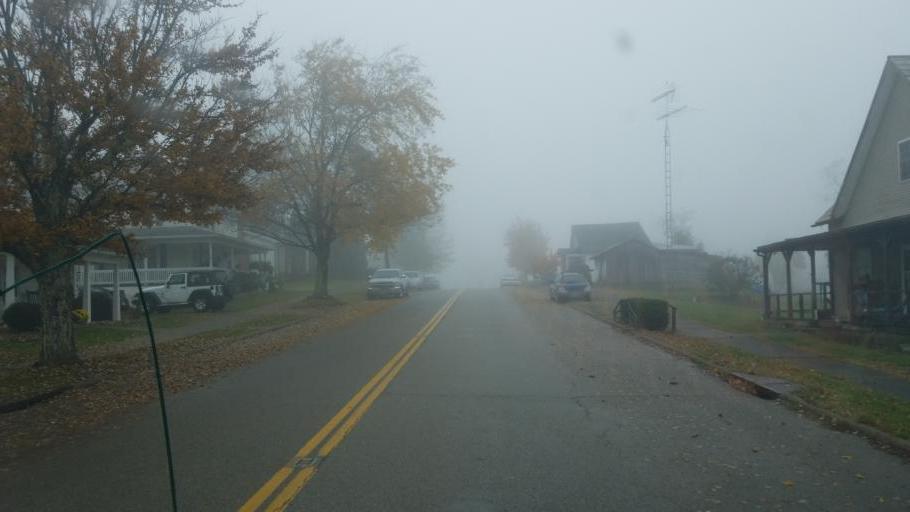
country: US
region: Ohio
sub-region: Morgan County
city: McConnelsville
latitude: 39.5764
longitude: -81.8571
